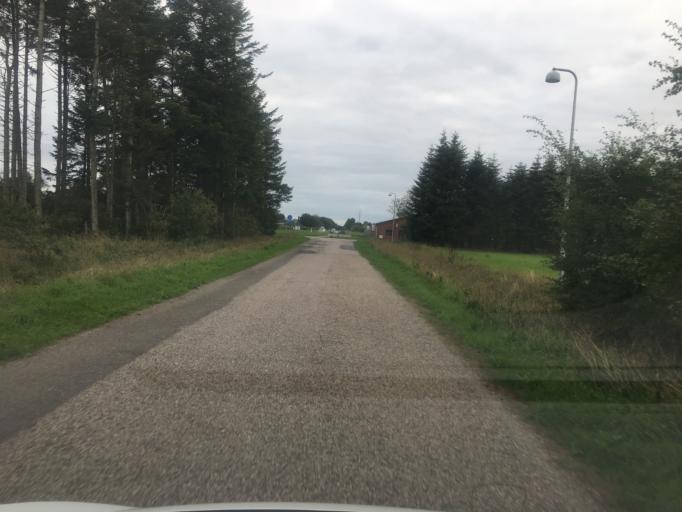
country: DK
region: South Denmark
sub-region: Tonder Kommune
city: Tonder
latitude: 54.9552
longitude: 8.9013
